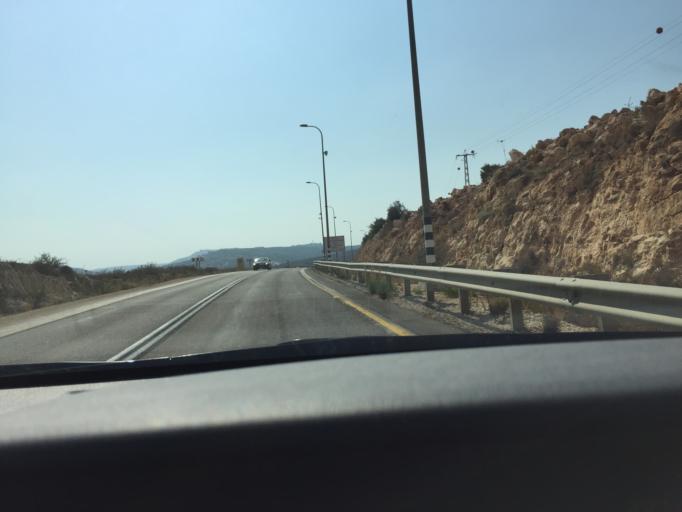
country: PS
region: West Bank
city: Bruqin
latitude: 32.0795
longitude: 35.0981
